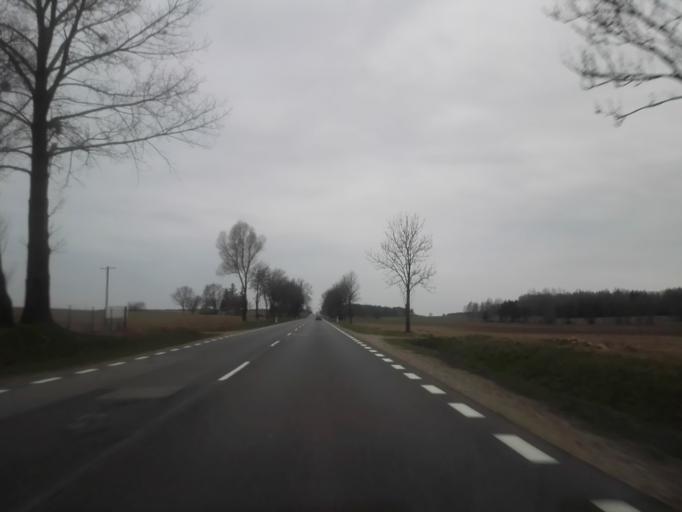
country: PL
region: Podlasie
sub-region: Powiat kolnenski
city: Stawiski
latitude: 53.4566
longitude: 22.1923
